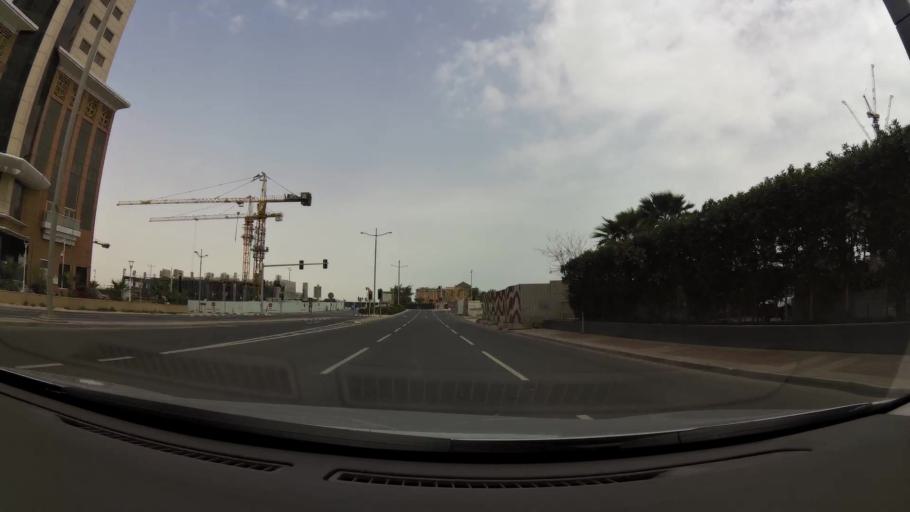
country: QA
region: Baladiyat ad Dawhah
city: Doha
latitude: 25.3291
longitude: 51.5296
